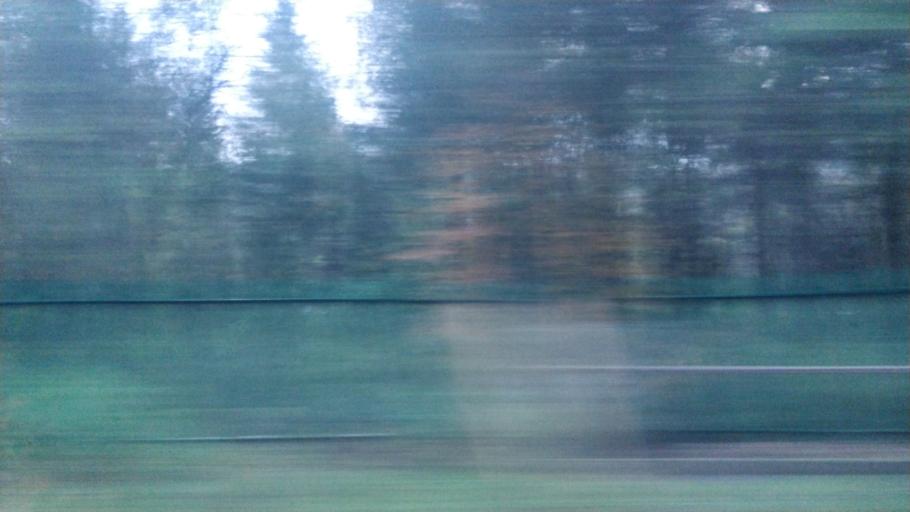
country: GB
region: England
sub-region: Lancashire
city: Parbold
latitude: 53.5849
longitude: -2.7458
